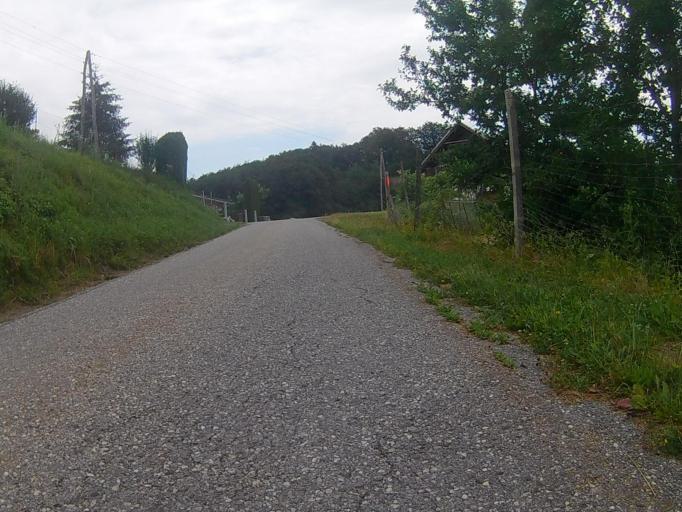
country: SI
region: Sentilj
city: Sentilj v Slov. Goricah
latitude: 46.6729
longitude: 15.6382
